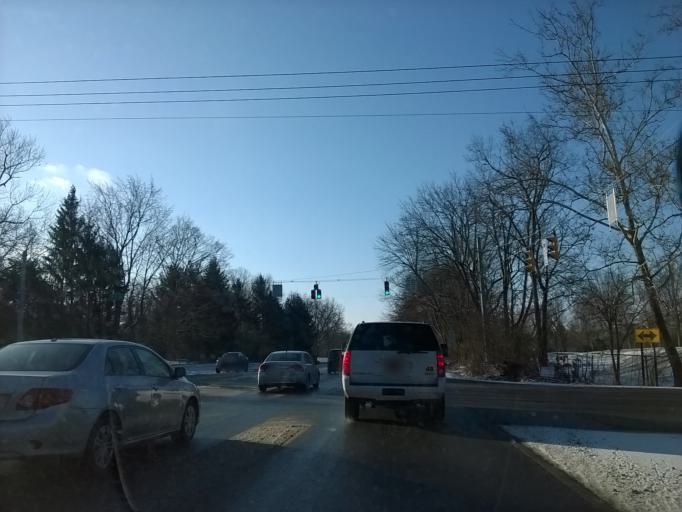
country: US
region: Indiana
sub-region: Marion County
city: Meridian Hills
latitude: 39.8833
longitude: -86.1579
